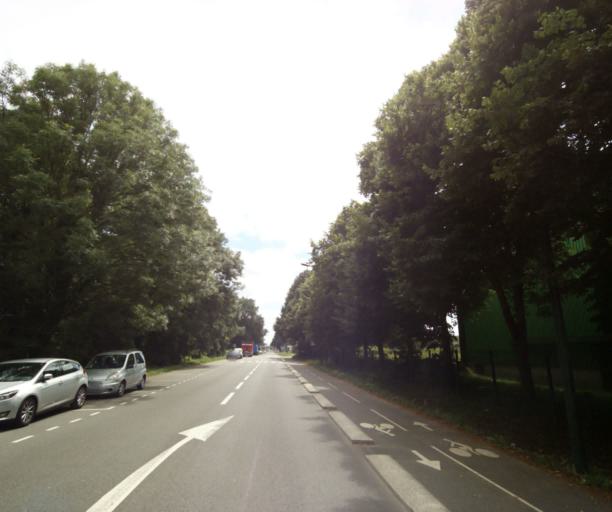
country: FR
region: Ile-de-France
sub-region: Departement des Yvelines
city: Saint-Cyr-l'Ecole
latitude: 48.7927
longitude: 2.0630
